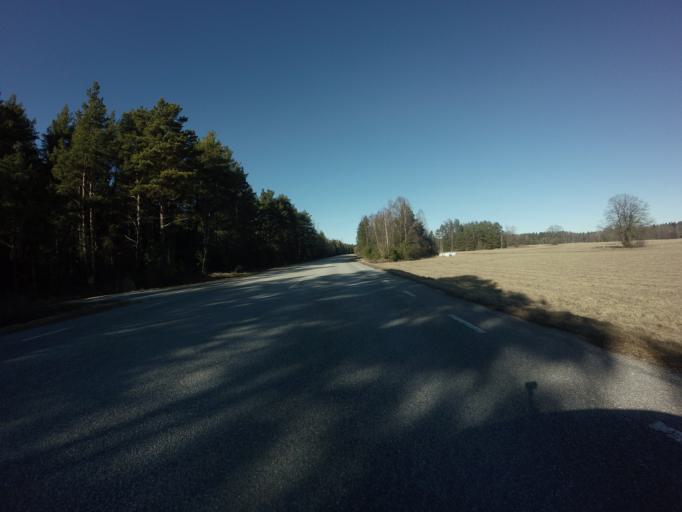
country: EE
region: Saare
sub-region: Kuressaare linn
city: Kuressaare
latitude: 58.4787
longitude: 22.2314
